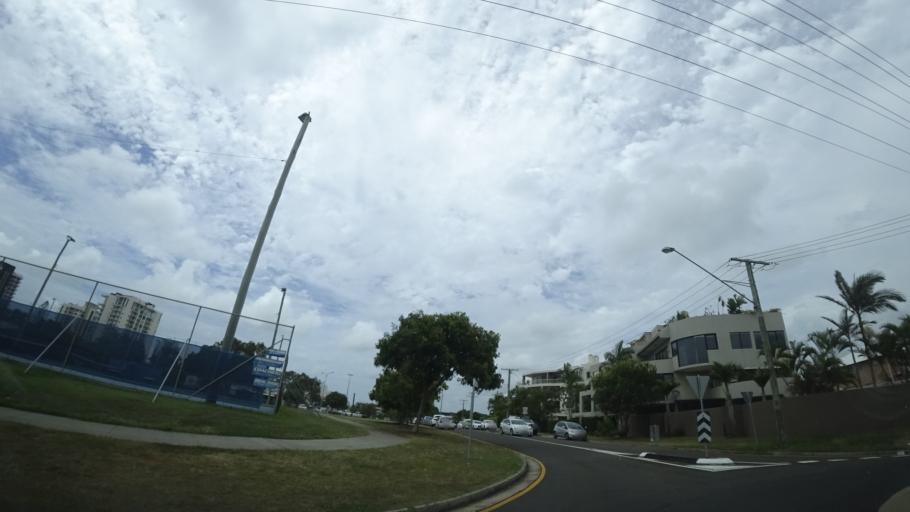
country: AU
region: Queensland
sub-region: Sunshine Coast
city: Mooloolaba
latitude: -26.6560
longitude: 153.0996
